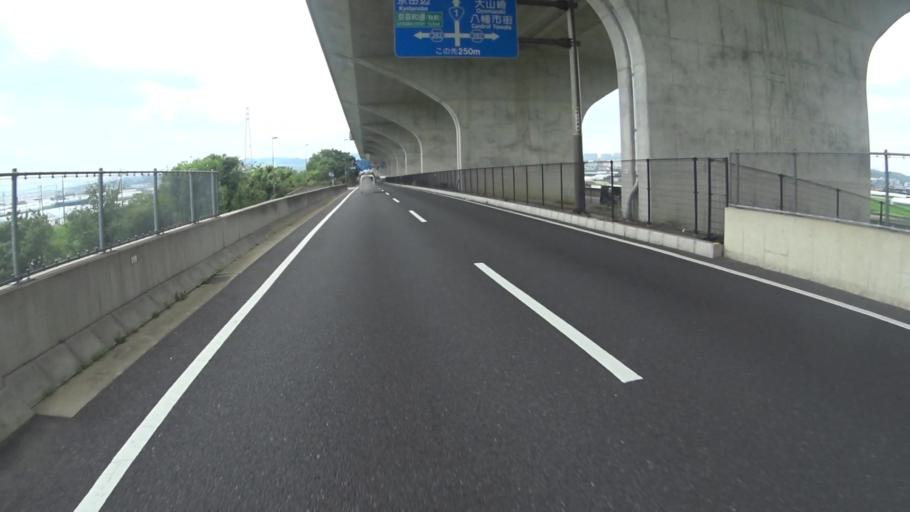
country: JP
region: Kyoto
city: Yawata
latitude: 34.8609
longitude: 135.7349
